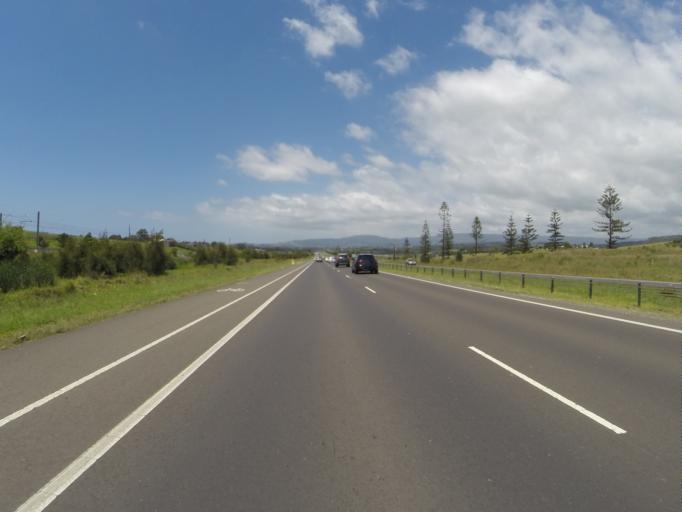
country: AU
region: New South Wales
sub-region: Shellharbour
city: Croom
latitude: -34.5952
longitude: 150.8427
